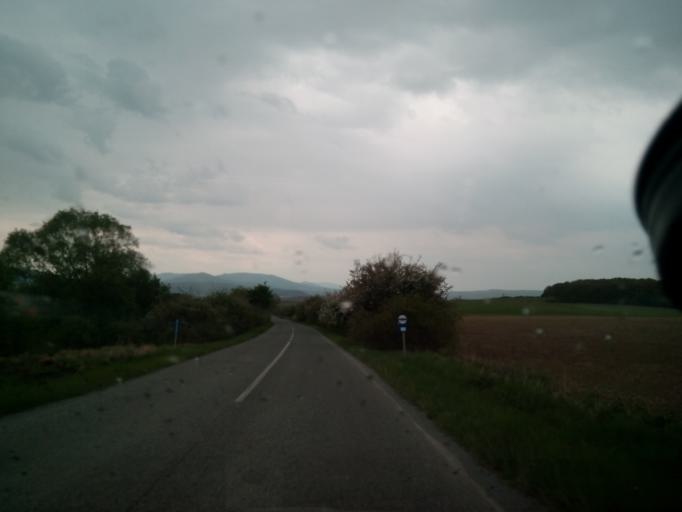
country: SK
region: Kosicky
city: Secovce
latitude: 48.7903
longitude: 21.4805
